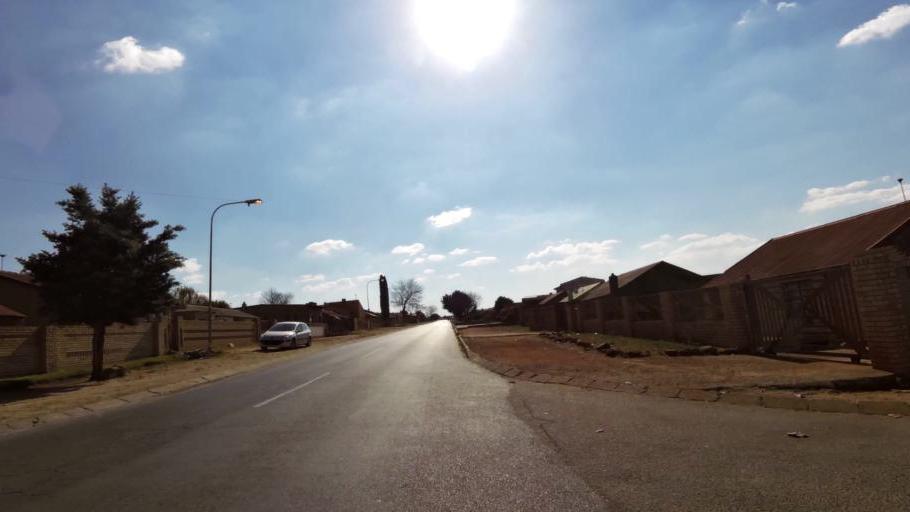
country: ZA
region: Gauteng
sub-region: City of Johannesburg Metropolitan Municipality
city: Soweto
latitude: -26.2379
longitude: 27.9118
